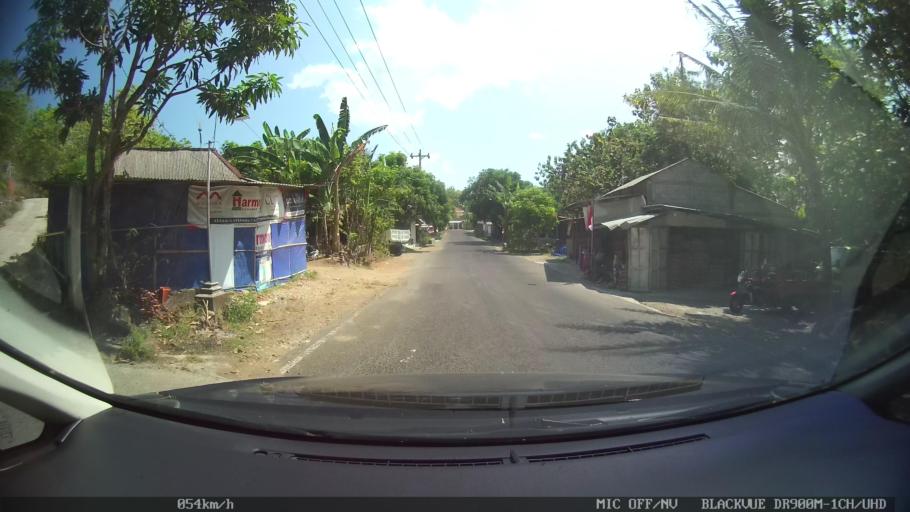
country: ID
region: Daerah Istimewa Yogyakarta
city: Pundong
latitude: -7.9589
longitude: 110.3597
